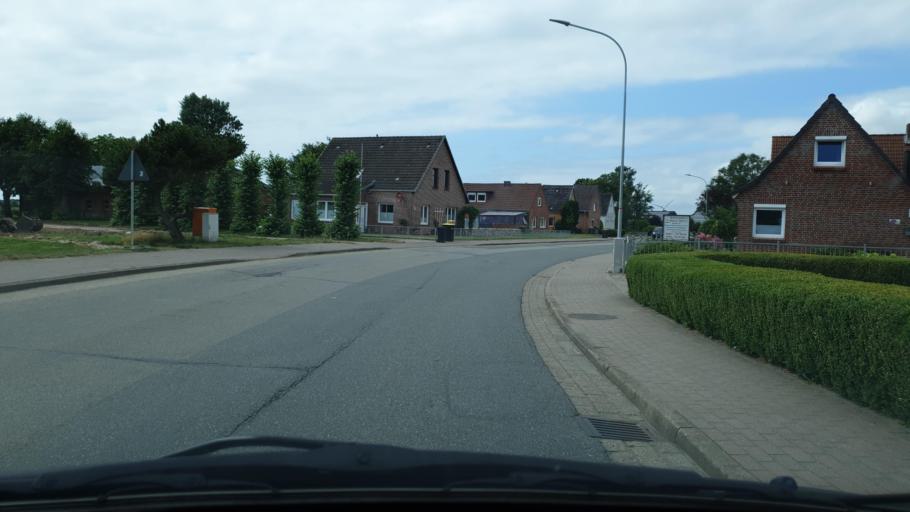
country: DE
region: Schleswig-Holstein
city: Marnerdeich
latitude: 53.9478
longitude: 8.9934
